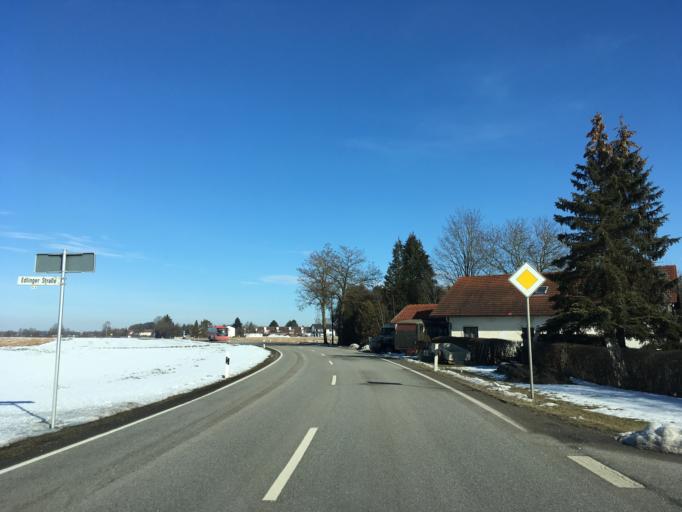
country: DE
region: Bavaria
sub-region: Upper Bavaria
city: Breitbrunn
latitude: 48.0495
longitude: 12.1581
